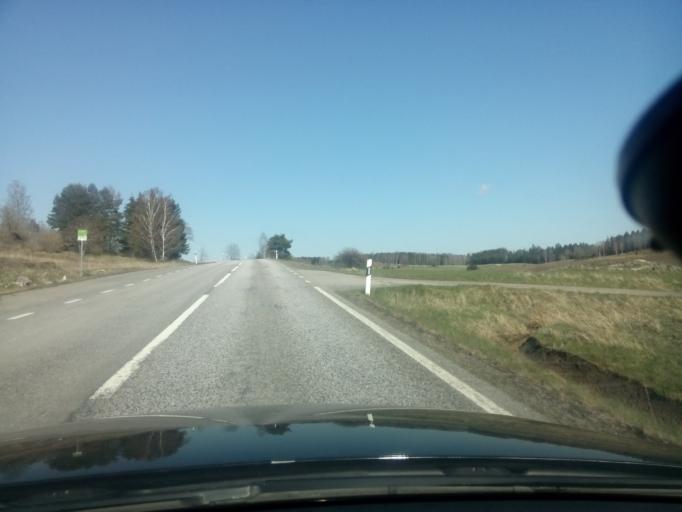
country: SE
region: Soedermanland
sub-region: Nykopings Kommun
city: Stigtomta
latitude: 58.9186
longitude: 16.8251
